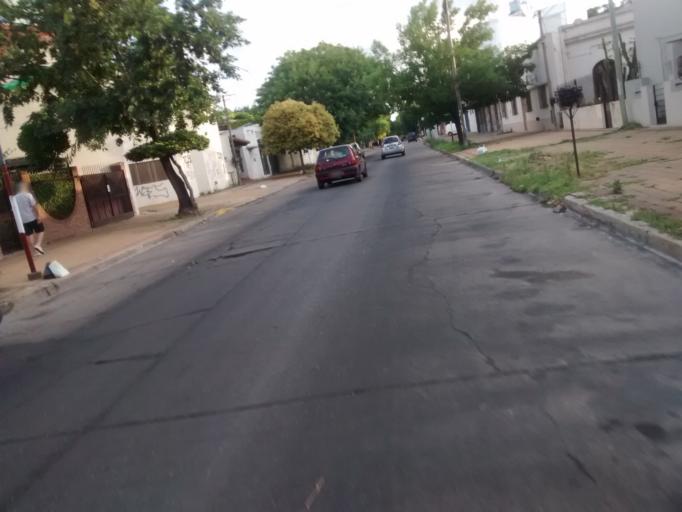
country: AR
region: Buenos Aires
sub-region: Partido de La Plata
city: La Plata
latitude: -34.9144
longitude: -57.9671
